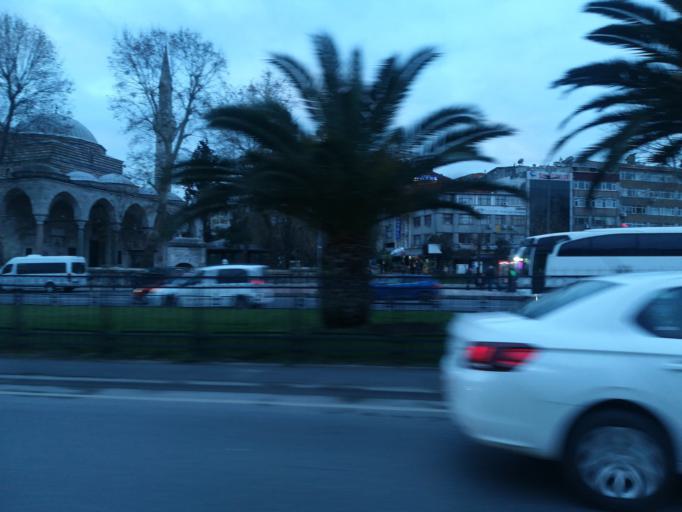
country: TR
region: Istanbul
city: Istanbul
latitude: 41.0111
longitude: 28.9490
